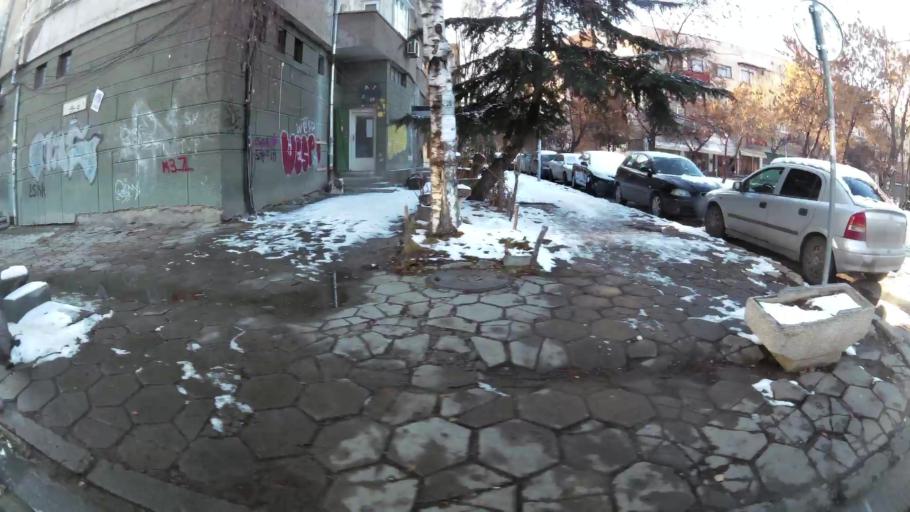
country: BG
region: Sofia-Capital
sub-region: Stolichna Obshtina
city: Sofia
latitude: 42.6812
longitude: 23.3609
